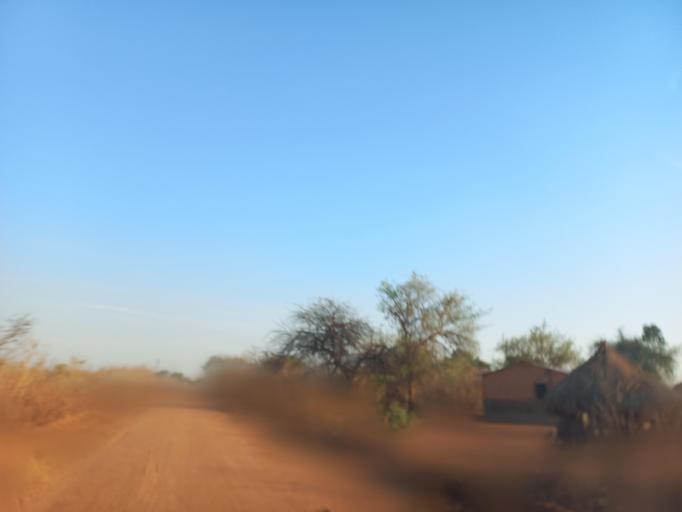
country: ZM
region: Lusaka
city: Luangwa
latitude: -15.4404
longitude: 30.3597
